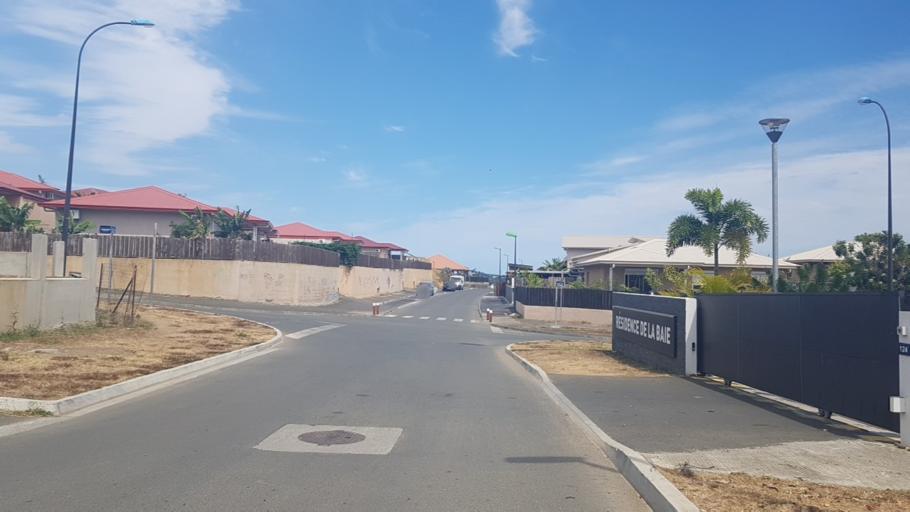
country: NC
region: South Province
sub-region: Dumbea
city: Dumbea
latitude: -22.2028
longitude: 166.4442
